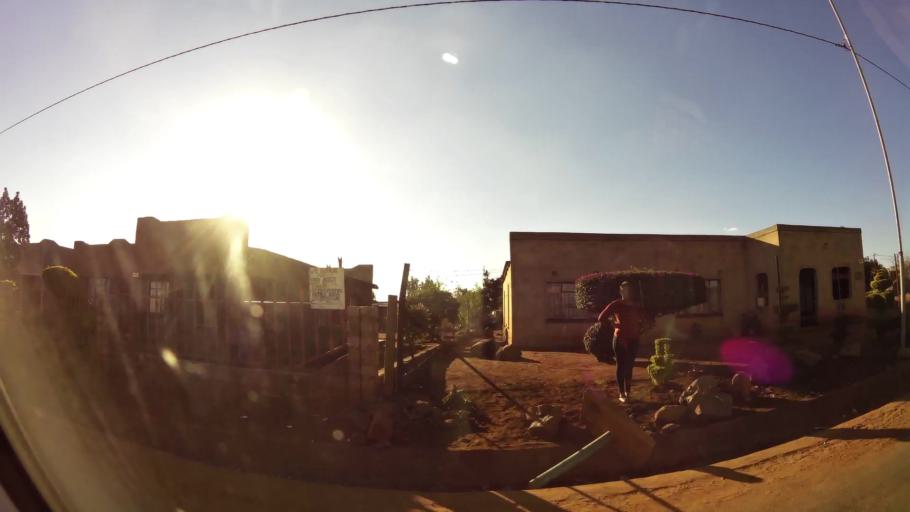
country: ZA
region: Limpopo
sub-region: Waterberg District Municipality
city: Mokopane
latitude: -24.1663
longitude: 28.9882
